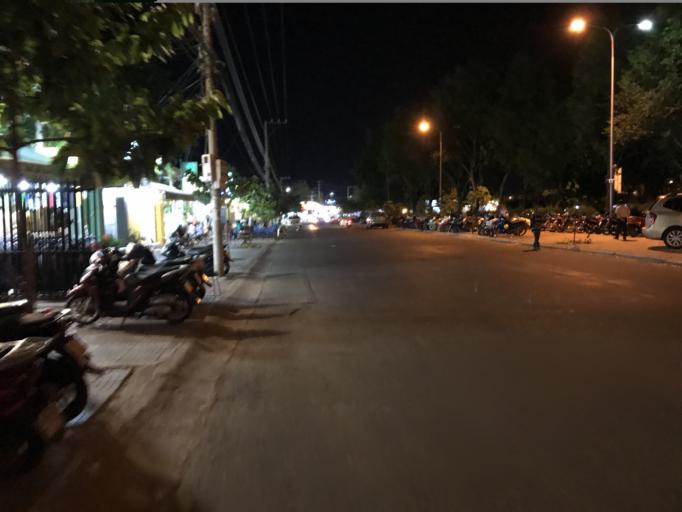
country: VN
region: Ninh Thuan
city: Phan Rang-Thap Cham
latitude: 11.5673
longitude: 108.9971
